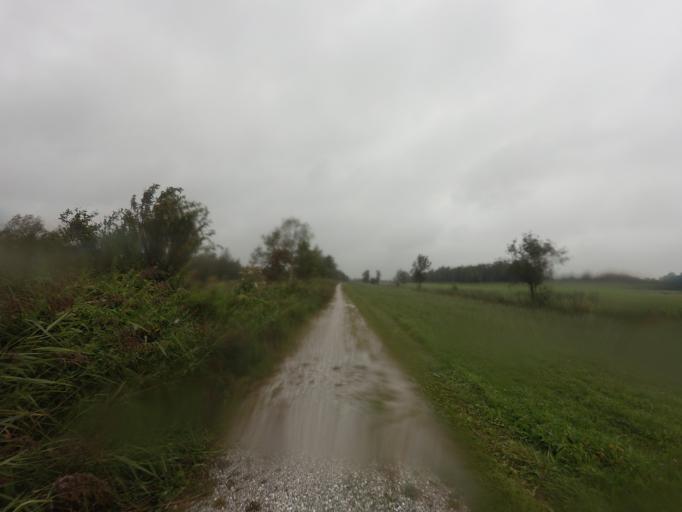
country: NL
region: Friesland
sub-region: Gemeente Smallingerland
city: Oudega
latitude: 53.0979
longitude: 5.9818
